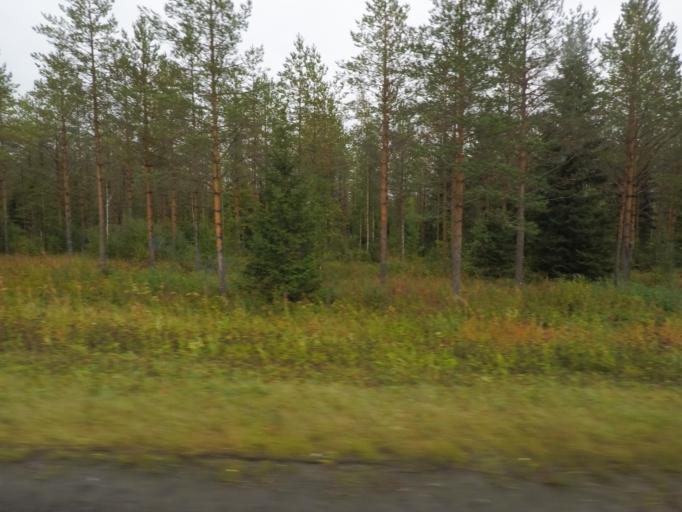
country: FI
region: Southern Savonia
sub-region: Pieksaemaeki
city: Juva
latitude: 61.9740
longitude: 27.8039
